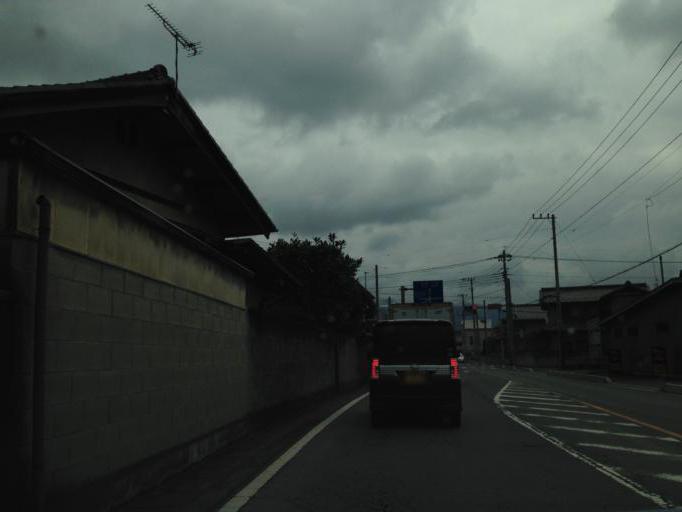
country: JP
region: Saitama
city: Chichibu
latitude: 36.0080
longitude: 139.0872
